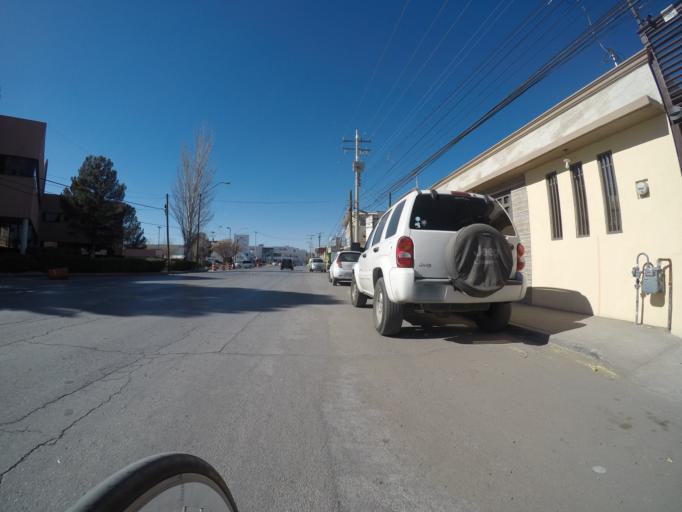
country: MX
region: Chihuahua
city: Ciudad Juarez
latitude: 31.7143
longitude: -106.4189
